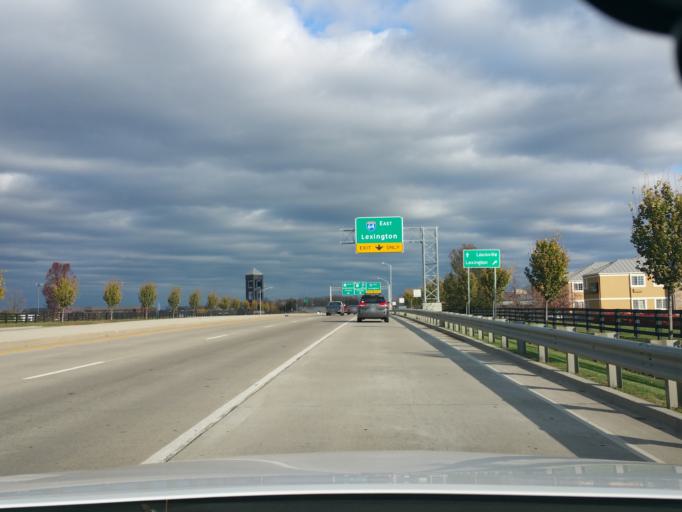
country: US
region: Kentucky
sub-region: Jefferson County
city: Douglass Hills
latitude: 38.2185
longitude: -85.5388
